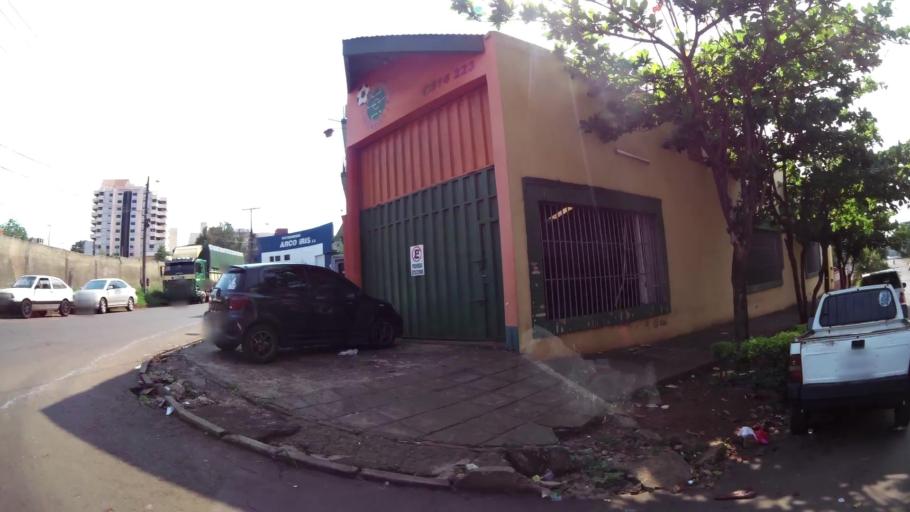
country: PY
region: Alto Parana
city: Ciudad del Este
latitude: -25.5084
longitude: -54.6202
